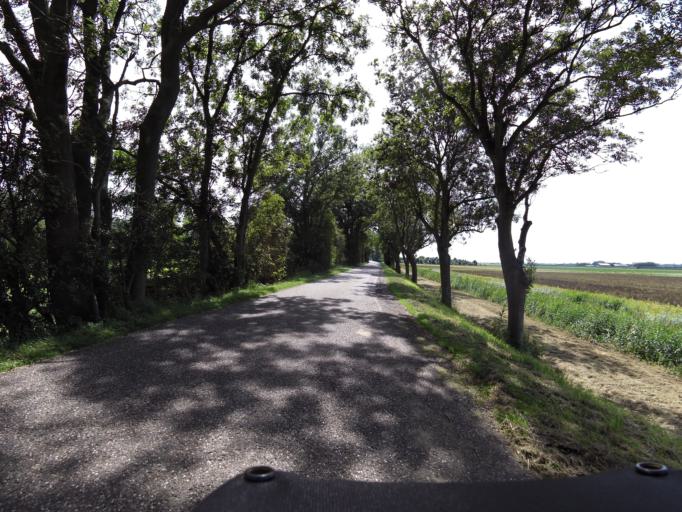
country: NL
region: South Holland
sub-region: Gemeente Goeree-Overflakkee
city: Dirksland
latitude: 51.7809
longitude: 4.1115
